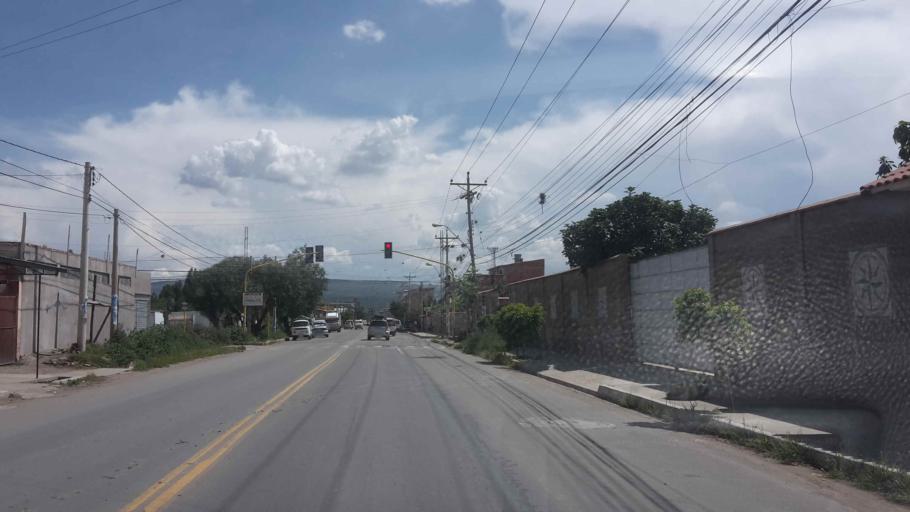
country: BO
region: Cochabamba
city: Cochabamba
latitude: -17.3814
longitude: -66.2357
